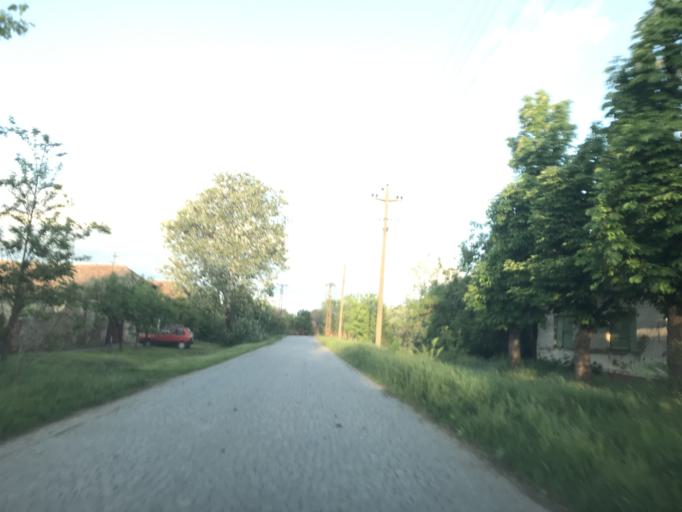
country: RS
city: Banatski Dvor
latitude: 45.5201
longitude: 20.5051
